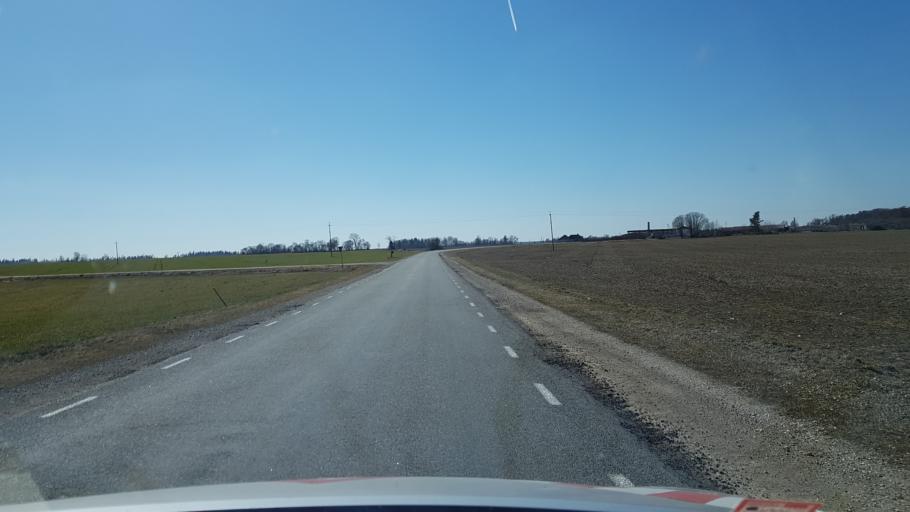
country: EE
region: Laeaene-Virumaa
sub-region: Vaeike-Maarja vald
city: Vaike-Maarja
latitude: 59.1151
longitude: 26.3586
